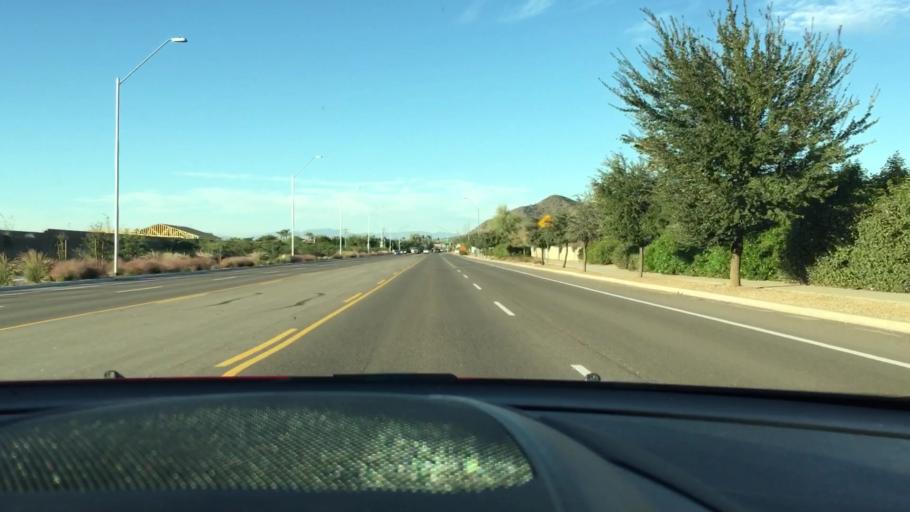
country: US
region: Arizona
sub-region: Maricopa County
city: Sun City West
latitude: 33.6931
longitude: -112.2551
